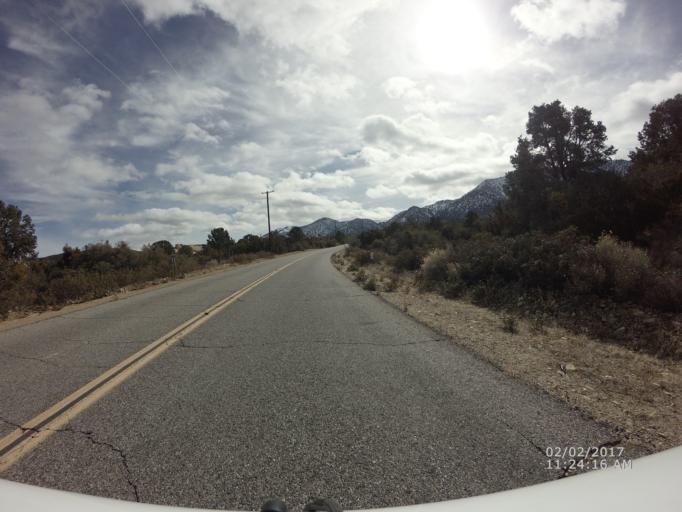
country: US
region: California
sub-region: Los Angeles County
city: Littlerock
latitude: 34.4290
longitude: -117.8714
